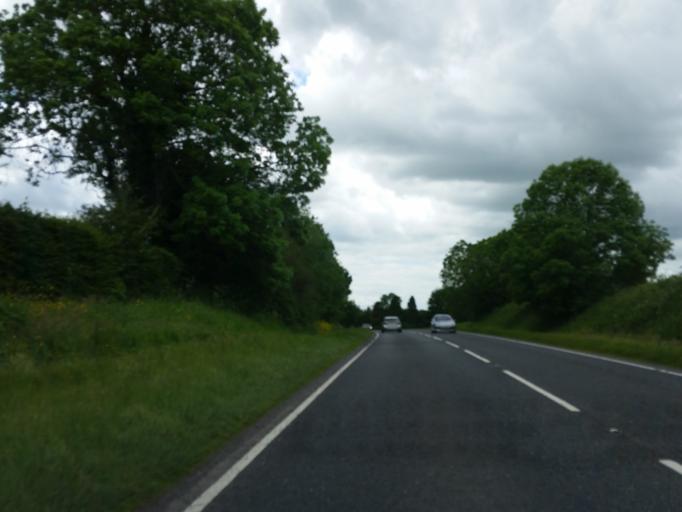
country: GB
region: Northern Ireland
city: Fivemiletown
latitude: 54.4257
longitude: -7.1366
